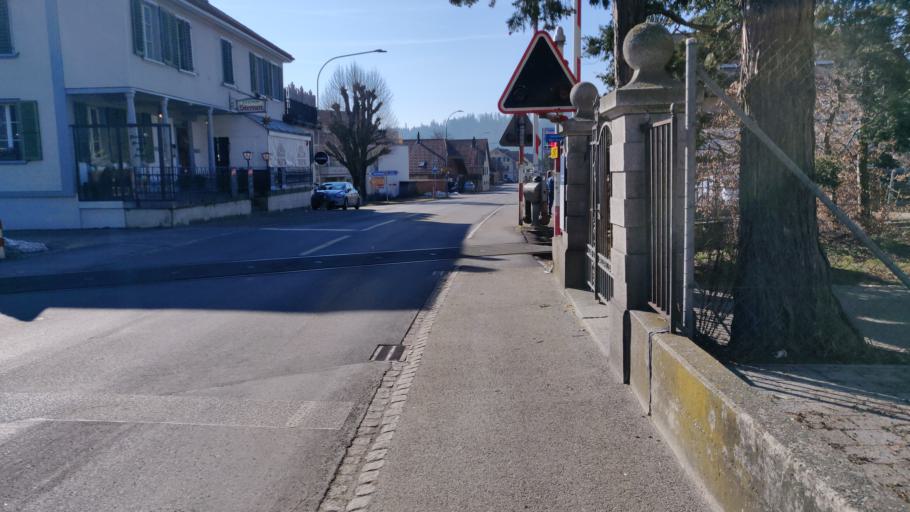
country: CH
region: Bern
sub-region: Emmental District
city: Sumiswald
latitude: 47.0252
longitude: 7.7418
